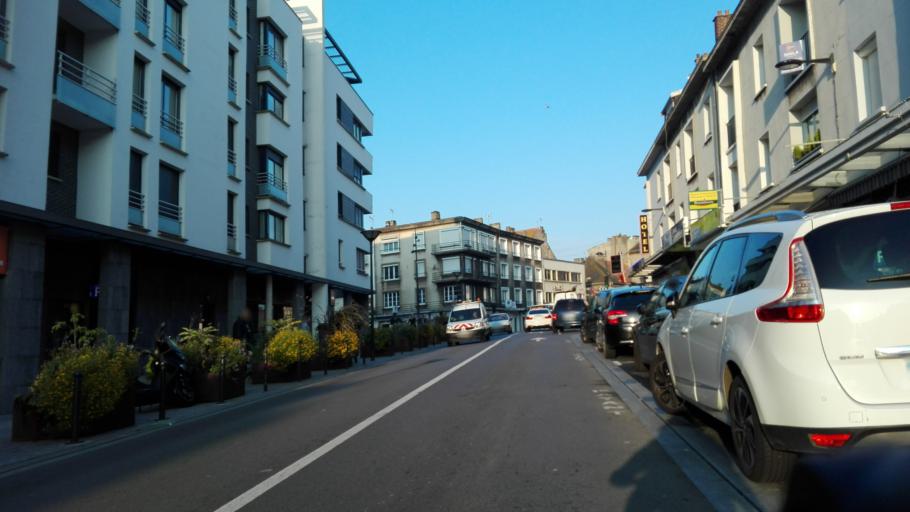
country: FR
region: Nord-Pas-de-Calais
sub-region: Departement du Pas-de-Calais
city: Boulogne-sur-Mer
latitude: 50.7220
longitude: 1.6082
